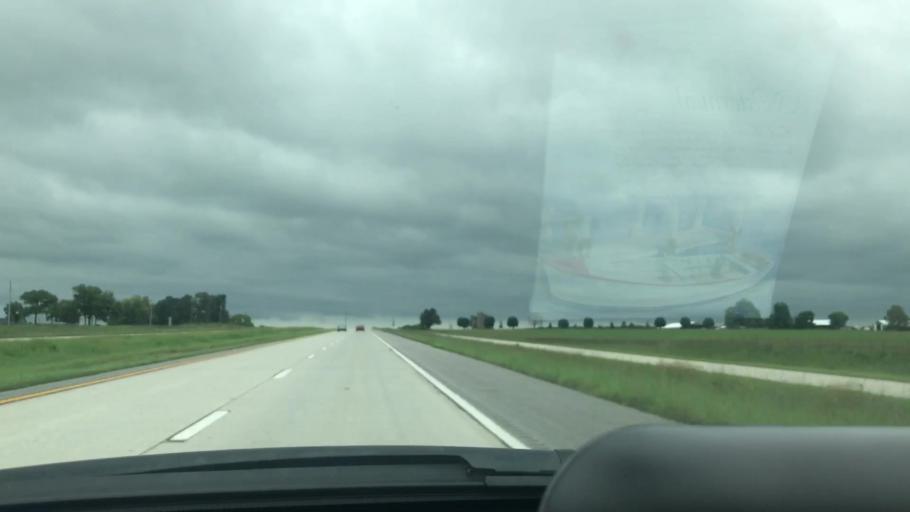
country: US
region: Missouri
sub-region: Greene County
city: Fair Grove
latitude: 37.4328
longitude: -93.1447
